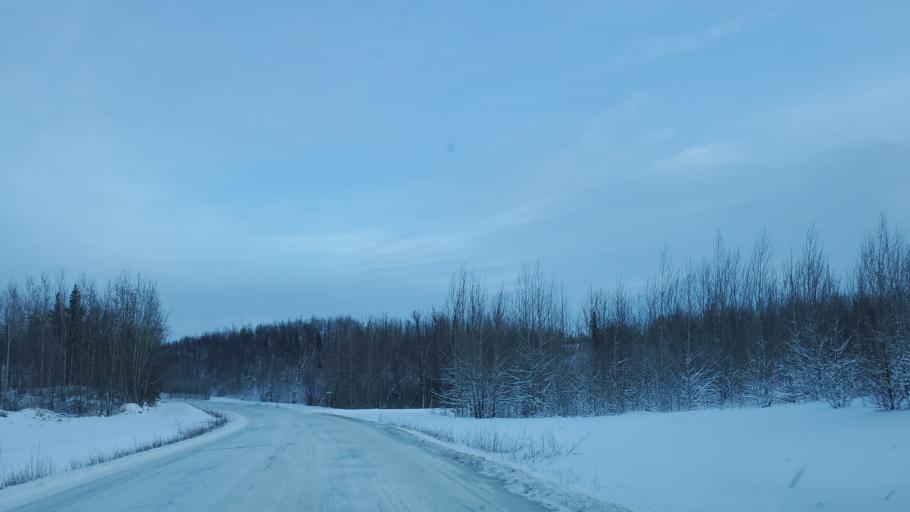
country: US
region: Alaska
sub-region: Matanuska-Susitna Borough
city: Lakes
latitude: 61.5482
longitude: -149.3132
